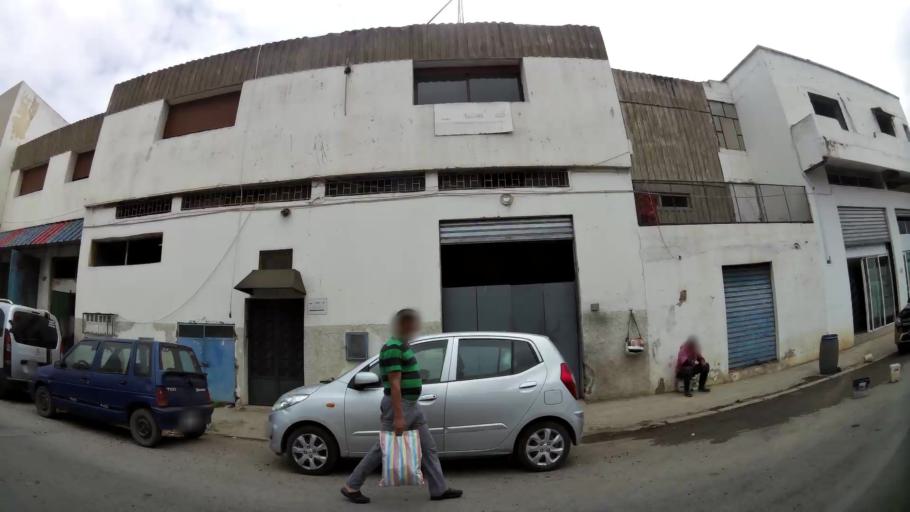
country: MA
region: Rabat-Sale-Zemmour-Zaer
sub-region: Rabat
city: Rabat
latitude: 33.9890
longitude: -6.8698
